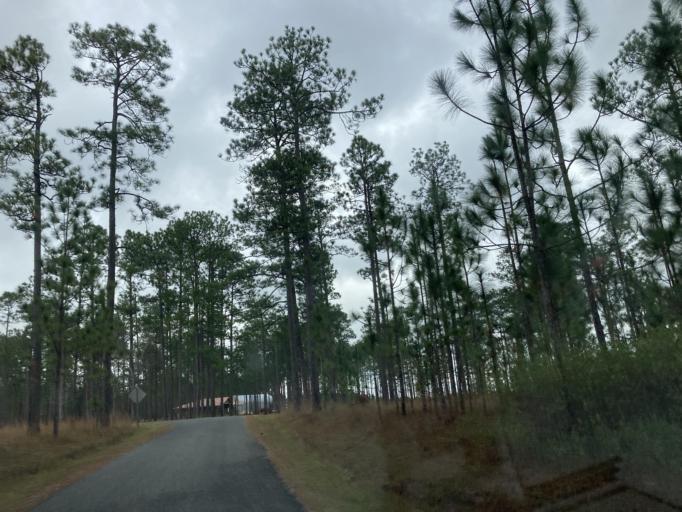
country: US
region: Mississippi
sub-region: Lamar County
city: Lumberton
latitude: 31.0947
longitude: -89.5303
